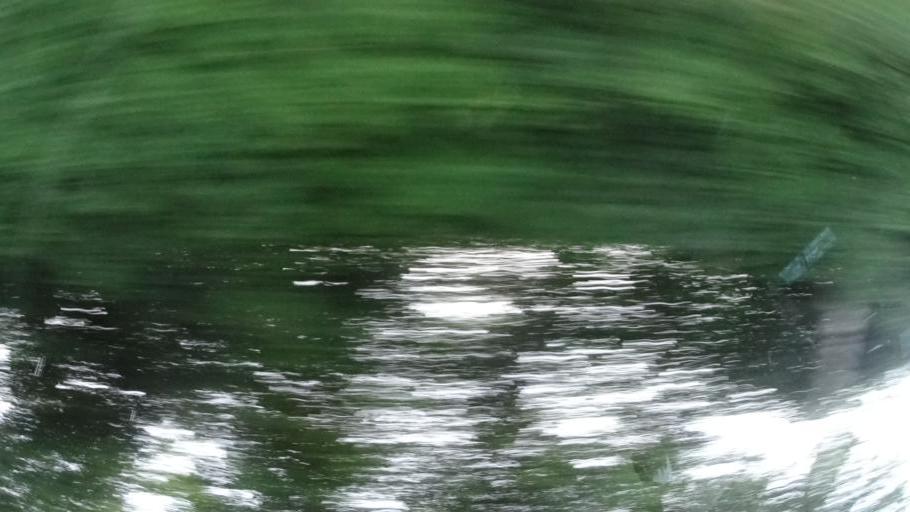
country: DE
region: Lower Saxony
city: Halle
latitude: 52.0266
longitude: 9.5581
